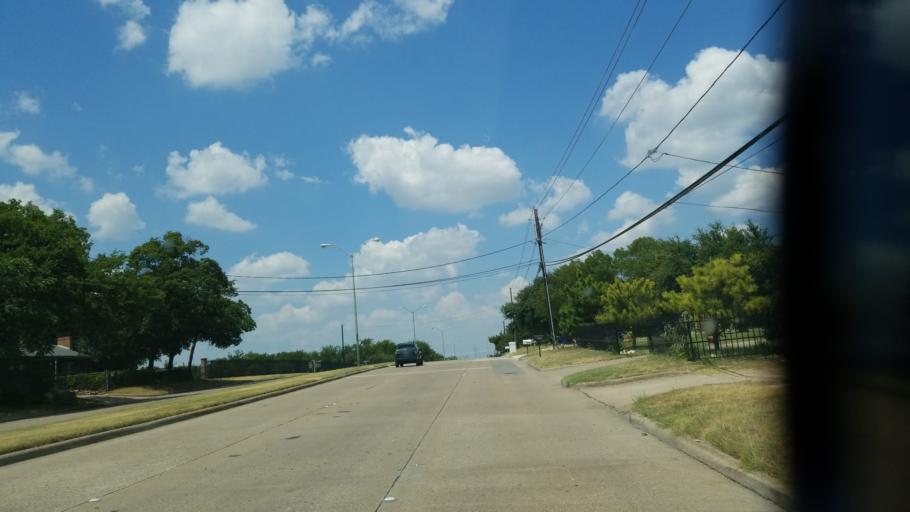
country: US
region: Texas
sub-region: Dallas County
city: Duncanville
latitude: 32.6728
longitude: -96.8913
